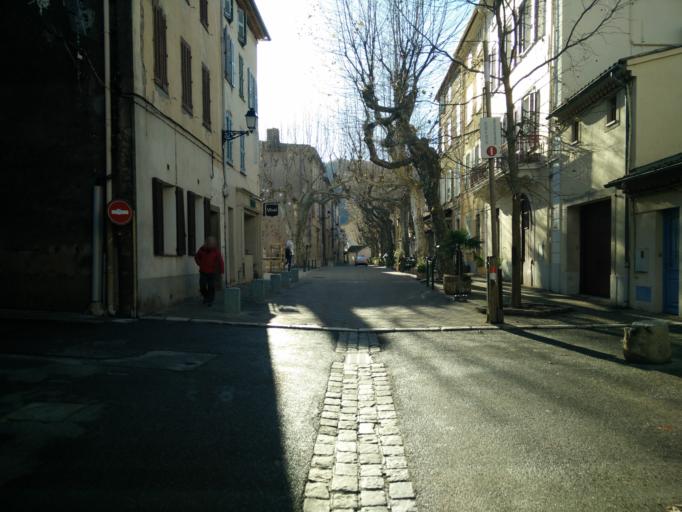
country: FR
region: Provence-Alpes-Cote d'Azur
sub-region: Departement du Var
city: Collobrieres
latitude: 43.2378
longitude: 6.3091
